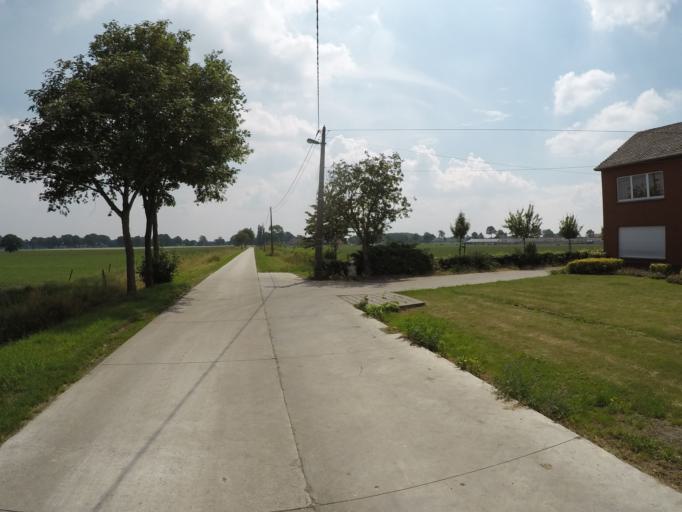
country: BE
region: Flanders
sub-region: Provincie Antwerpen
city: Rijkevorsel
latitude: 51.3629
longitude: 4.7332
